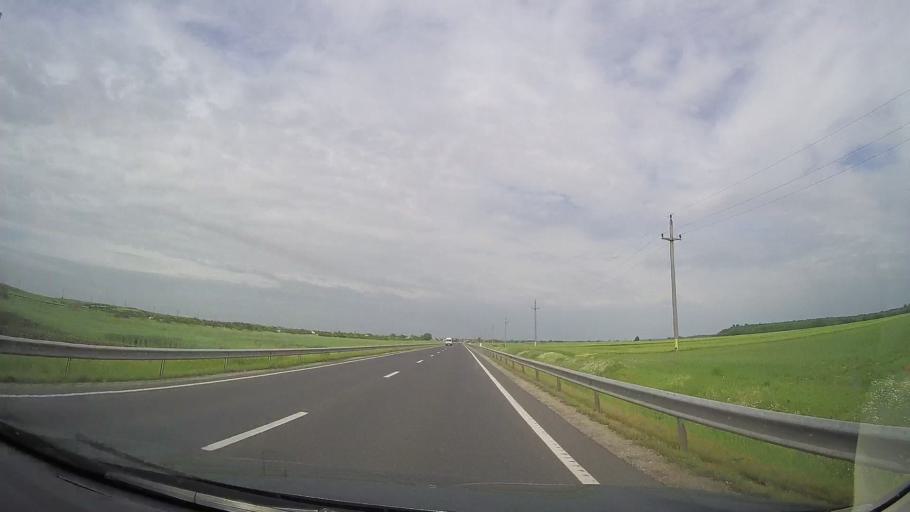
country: RO
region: Teleorman
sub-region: Comuna Nenciulesti
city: Nenciulesti
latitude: 44.0199
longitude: 25.1807
